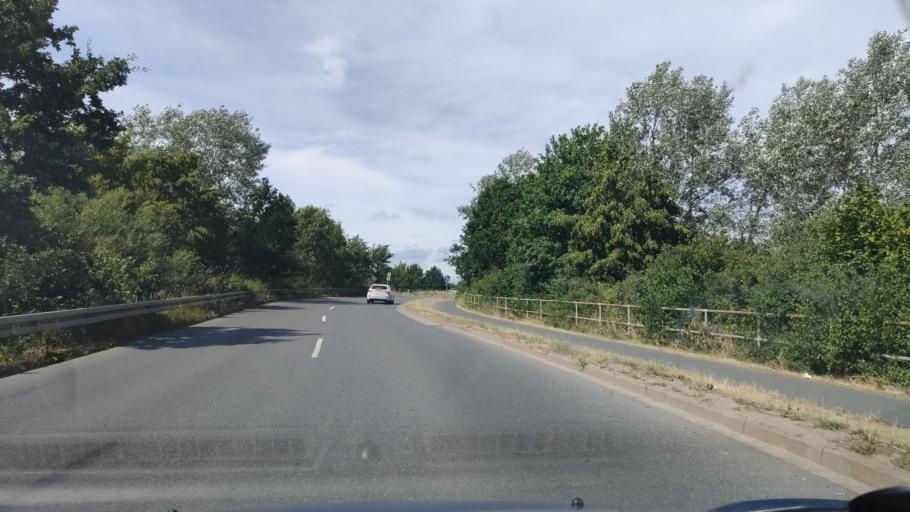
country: DE
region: Lower Saxony
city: Ronnenberg
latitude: 52.3487
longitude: 9.6552
